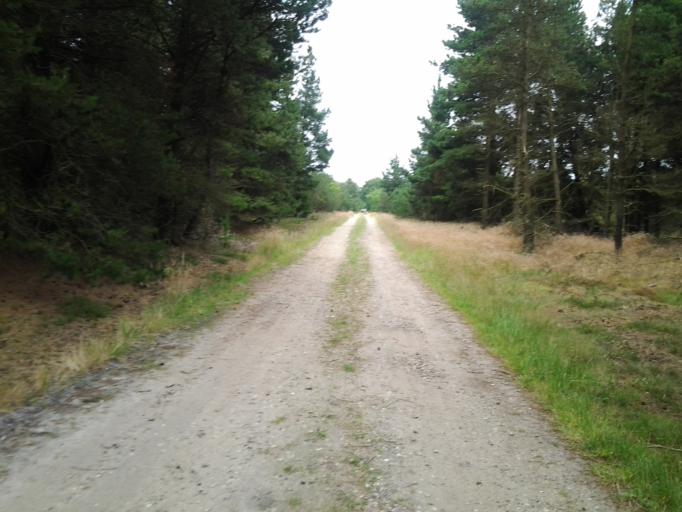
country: DE
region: Schleswig-Holstein
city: List
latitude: 55.1179
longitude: 8.5422
